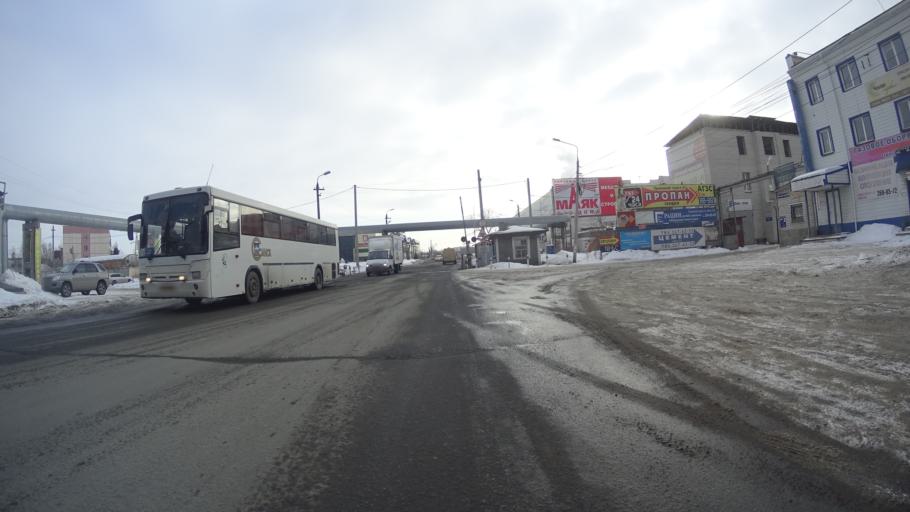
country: RU
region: Chelyabinsk
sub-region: Gorod Chelyabinsk
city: Chelyabinsk
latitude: 55.1210
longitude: 61.3861
